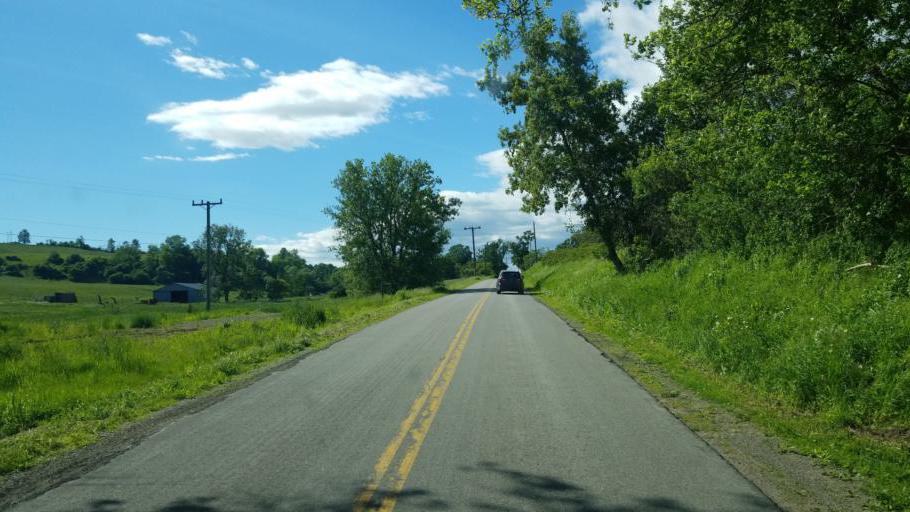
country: US
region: New York
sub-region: Montgomery County
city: Fort Plain
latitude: 42.9583
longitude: -74.6366
